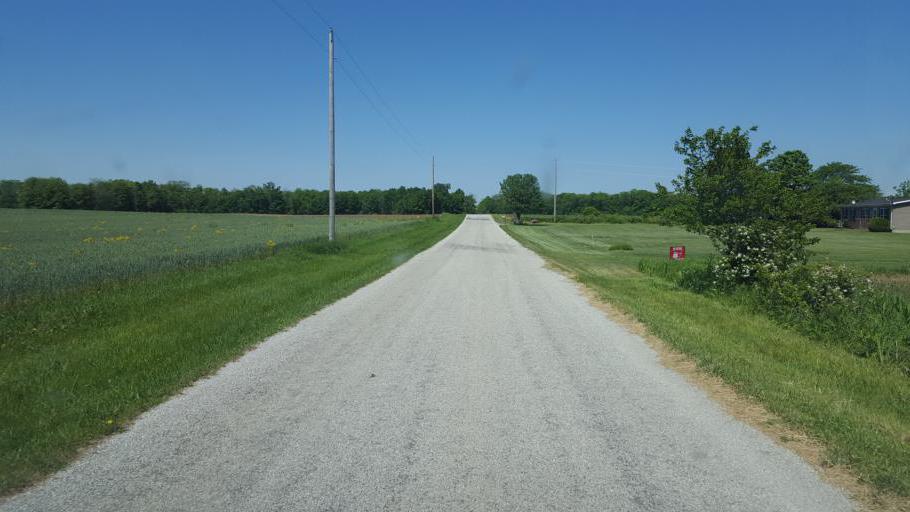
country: US
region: Ohio
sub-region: Hardin County
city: Forest
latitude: 40.6727
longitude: -83.3941
